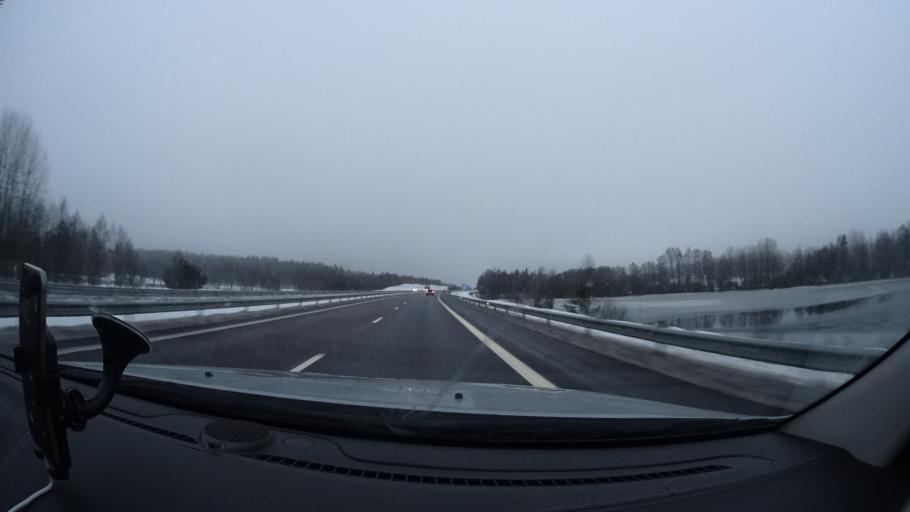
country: SE
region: Kronoberg
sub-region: Markaryds Kommun
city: Stromsnasbruk
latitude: 56.6388
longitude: 13.7986
